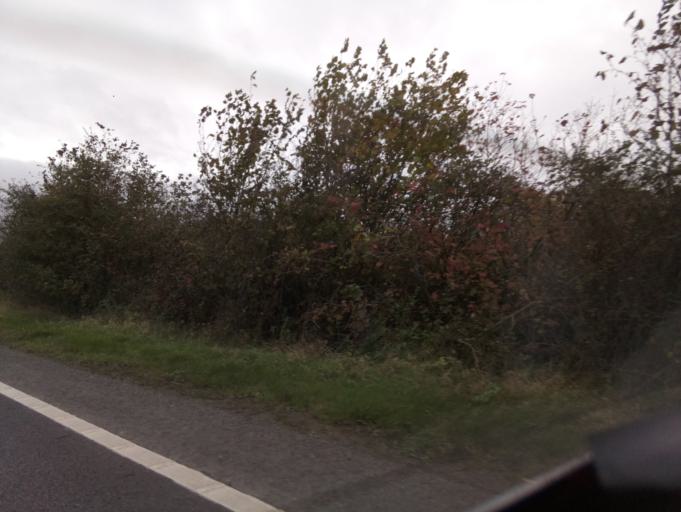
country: GB
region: England
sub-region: Somerset
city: Stoke-sub-Hamdon
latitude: 50.9732
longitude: -2.7324
